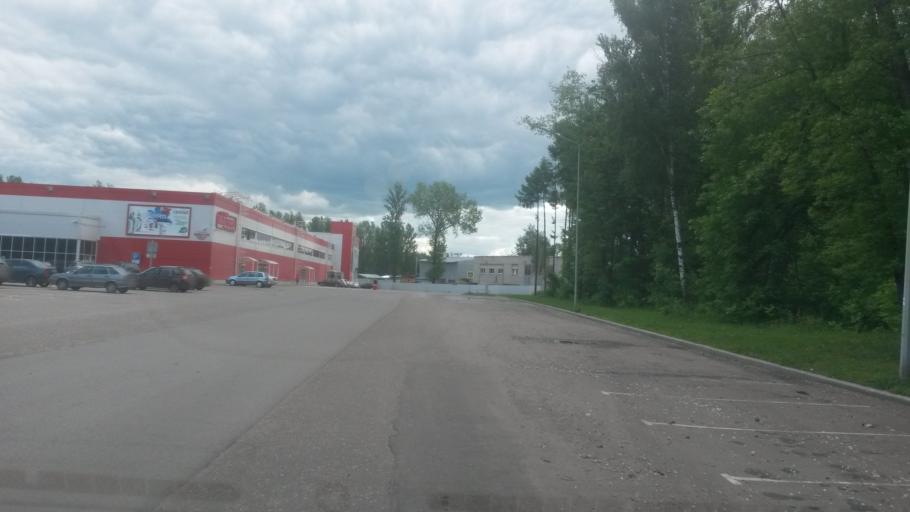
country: RU
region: Jaroslavl
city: Yaroslavl
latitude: 57.6787
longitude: 39.8035
